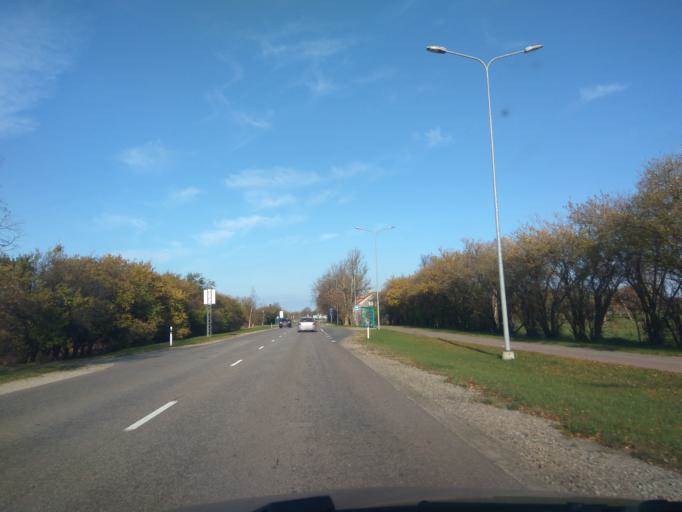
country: LV
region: Ventspils
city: Ventspils
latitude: 57.3643
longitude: 21.5634
